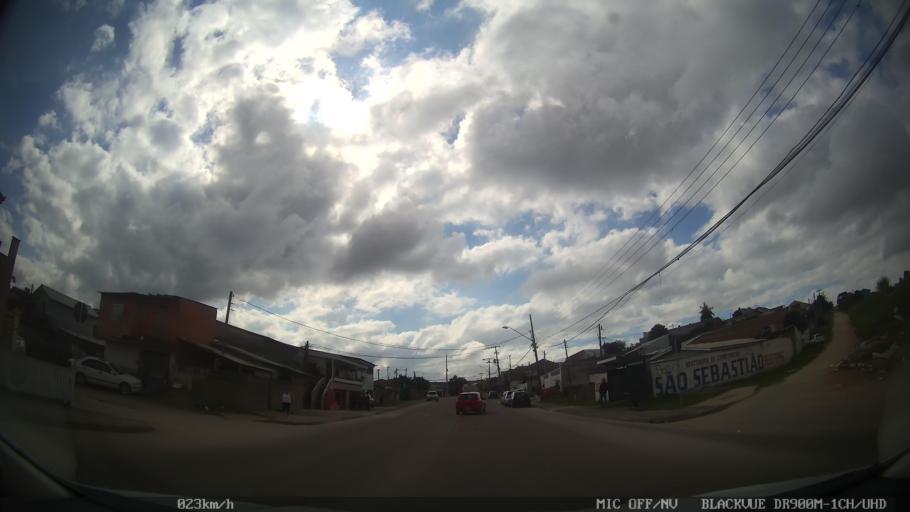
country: BR
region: Parana
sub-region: Colombo
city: Colombo
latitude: -25.3629
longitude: -49.1961
